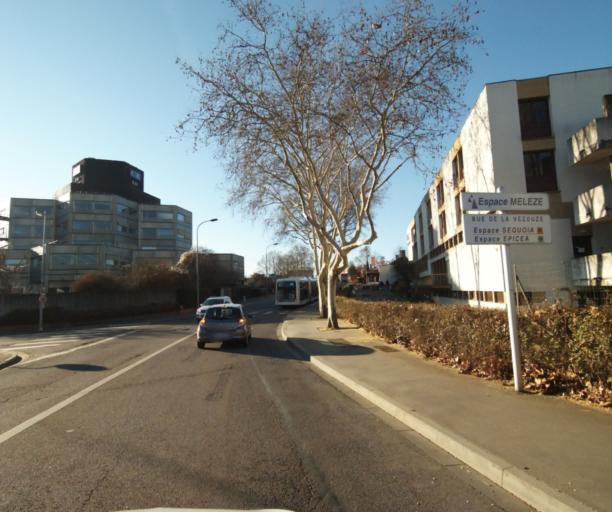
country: FR
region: Lorraine
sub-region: Departement de Meurthe-et-Moselle
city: Laxou
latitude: 48.6955
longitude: 6.1318
